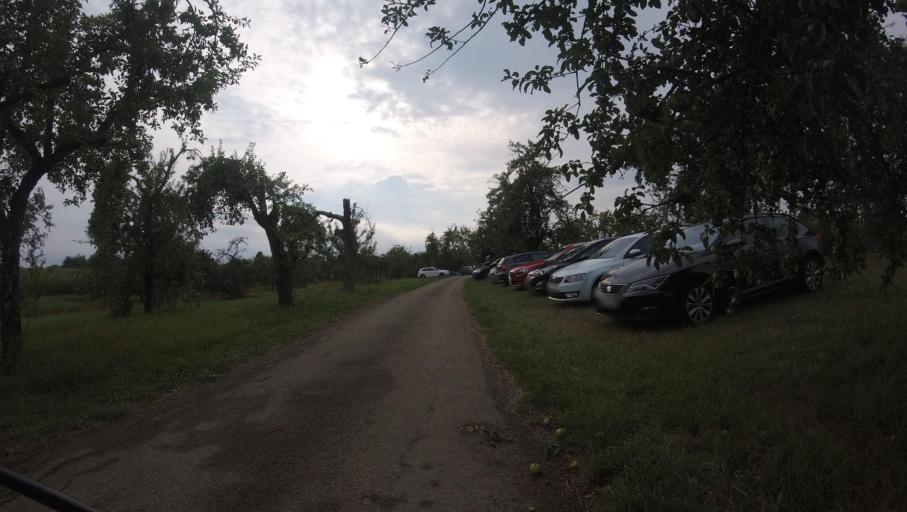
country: DE
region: Baden-Wuerttemberg
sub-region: Regierungsbezirk Stuttgart
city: Aspach
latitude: 48.9738
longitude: 9.3953
